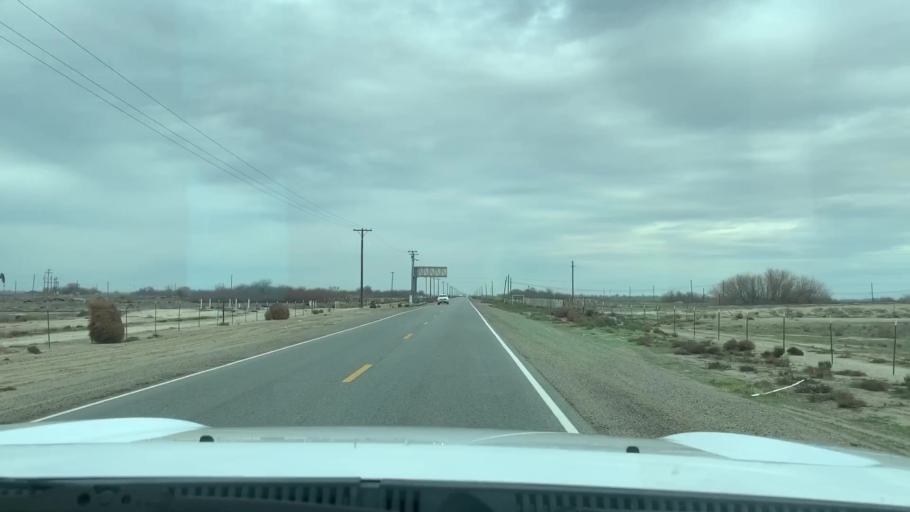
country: US
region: California
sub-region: Kern County
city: Rosedale
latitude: 35.3172
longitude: -119.2524
